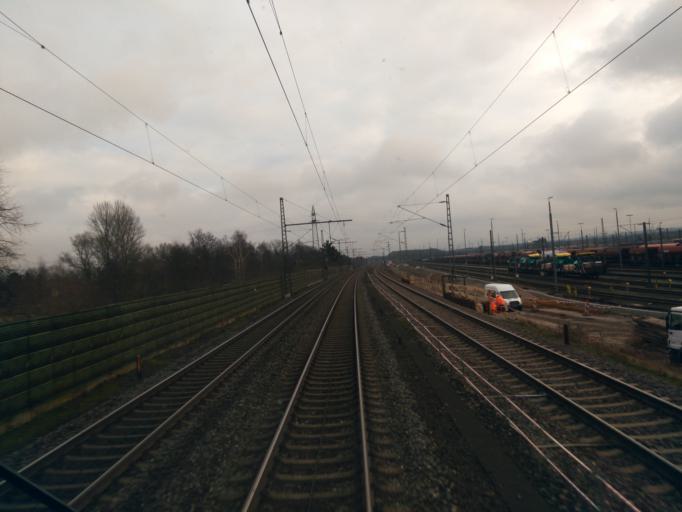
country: DE
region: Lower Saxony
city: Stelle
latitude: 53.4123
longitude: 10.0524
